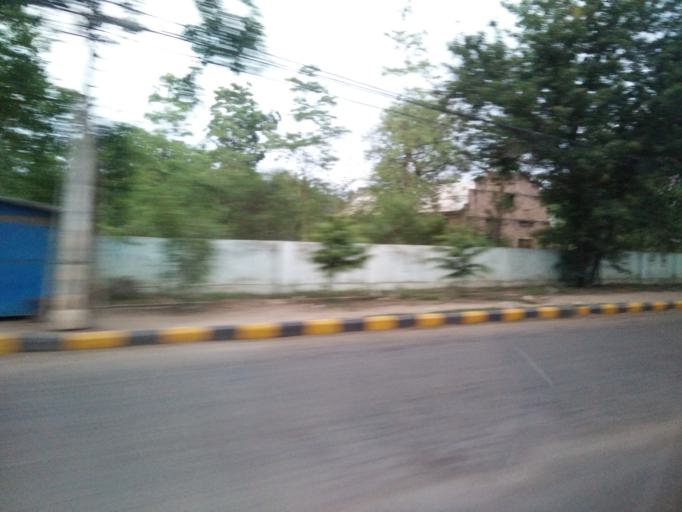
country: MM
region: Magway
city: Pakokku
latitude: 21.3315
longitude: 95.0730
